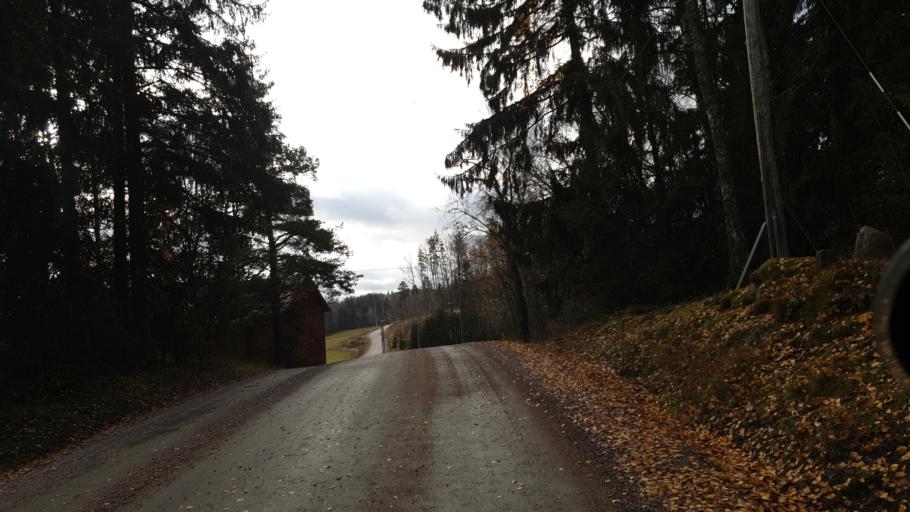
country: FI
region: Uusimaa
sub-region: Helsinki
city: Siuntio
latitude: 60.2382
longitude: 24.3047
